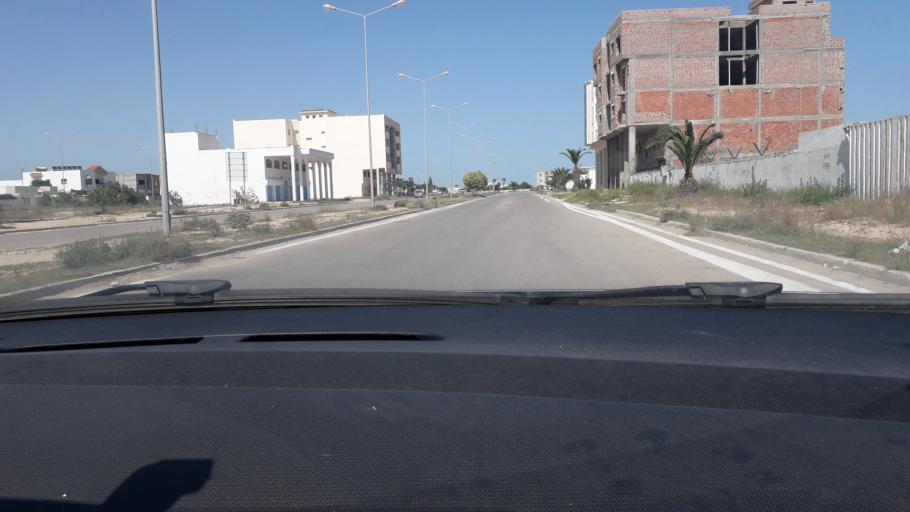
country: TN
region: Safaqis
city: Al Qarmadah
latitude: 34.8352
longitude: 10.7624
